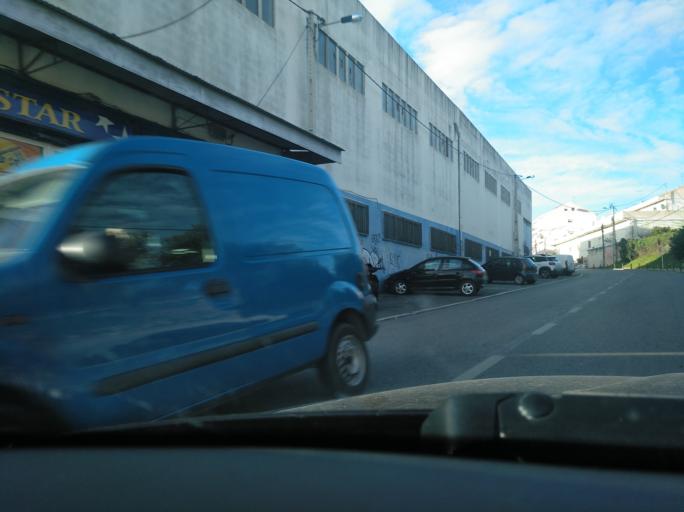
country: PT
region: Lisbon
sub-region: Loures
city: Unhos
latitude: 38.8177
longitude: -9.1185
